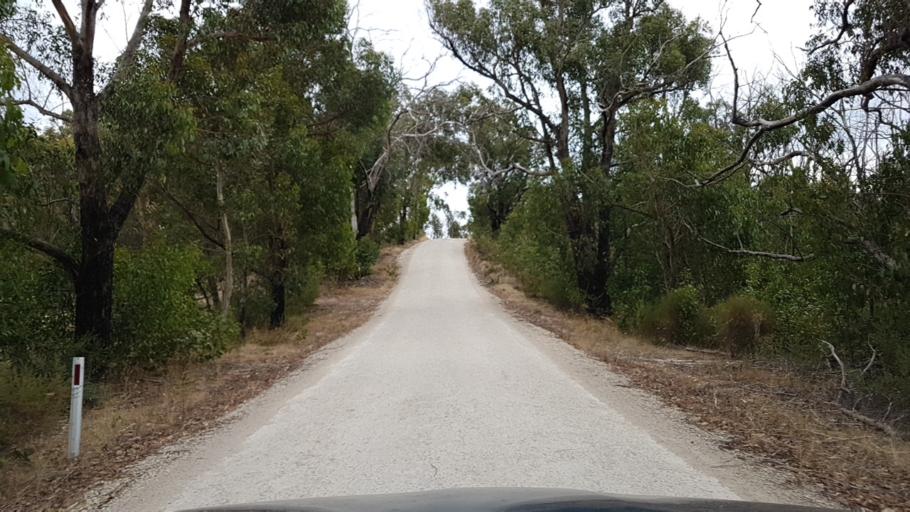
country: AU
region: South Australia
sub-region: Tea Tree Gully
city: Golden Grove
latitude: -34.7820
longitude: 138.8138
